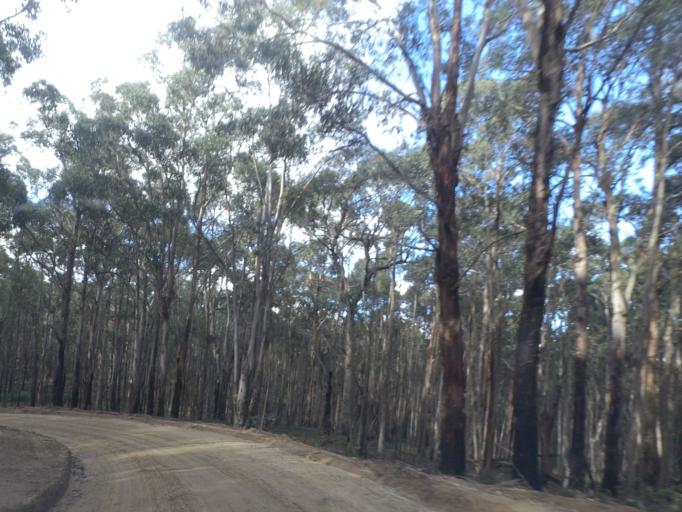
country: AU
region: Victoria
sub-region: Moorabool
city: Bacchus Marsh
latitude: -37.4525
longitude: 144.4600
